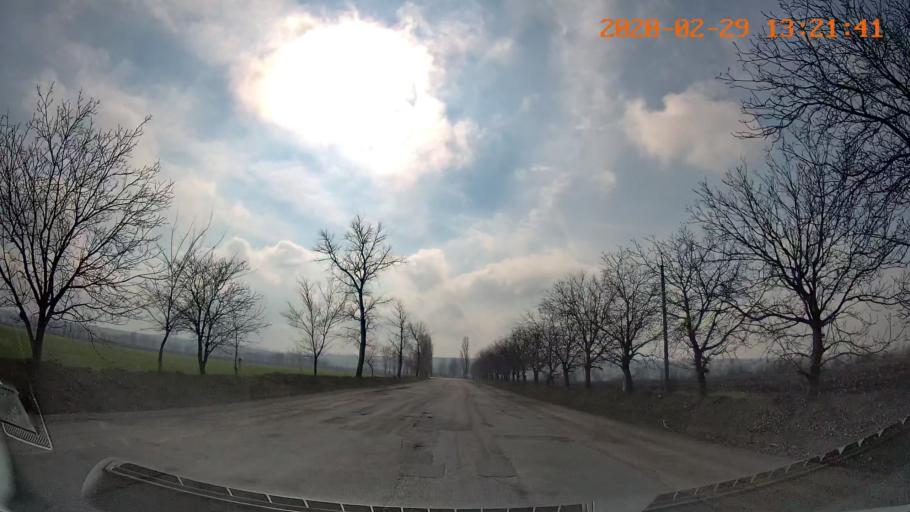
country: MD
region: Telenesti
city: Camenca
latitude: 47.9680
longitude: 28.6307
